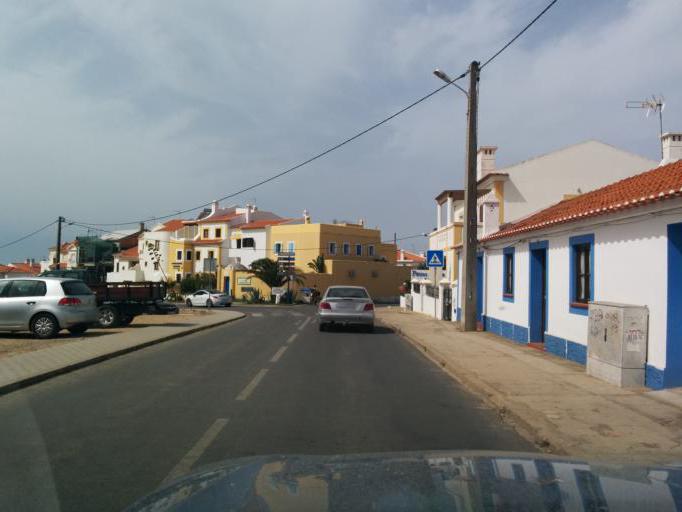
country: PT
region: Beja
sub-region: Odemira
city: Vila Nova de Milfontes
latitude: 37.7250
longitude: -8.7849
